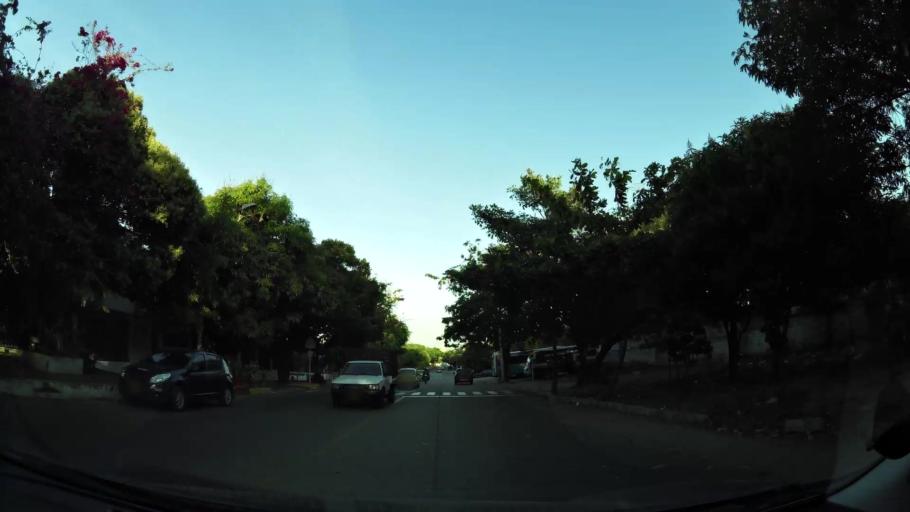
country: CO
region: Atlantico
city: Barranquilla
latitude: 10.9726
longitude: -74.7998
